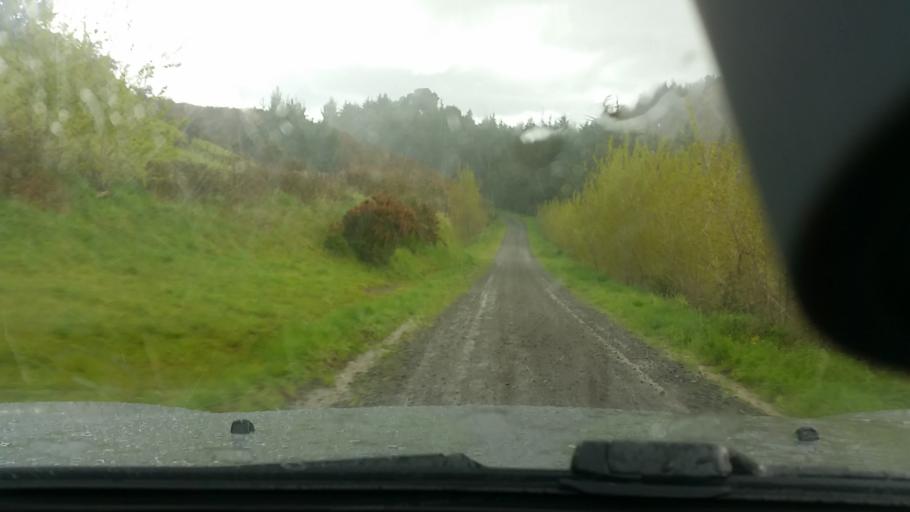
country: NZ
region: Waikato
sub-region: Taupo District
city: Taupo
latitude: -38.4854
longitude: 176.2107
